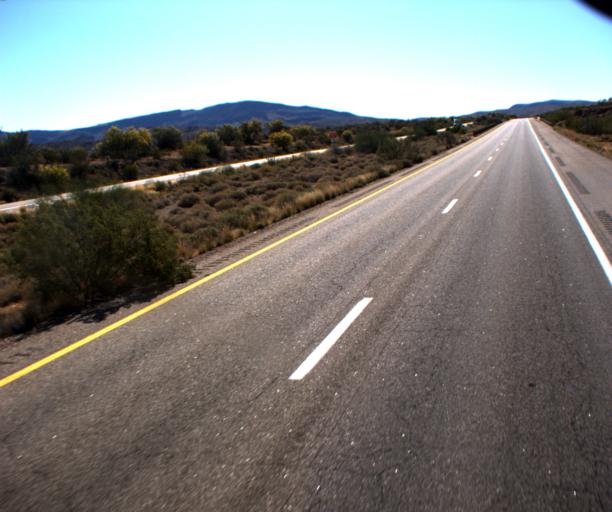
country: US
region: Arizona
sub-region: Yavapai County
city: Bagdad
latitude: 34.6324
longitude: -113.5486
